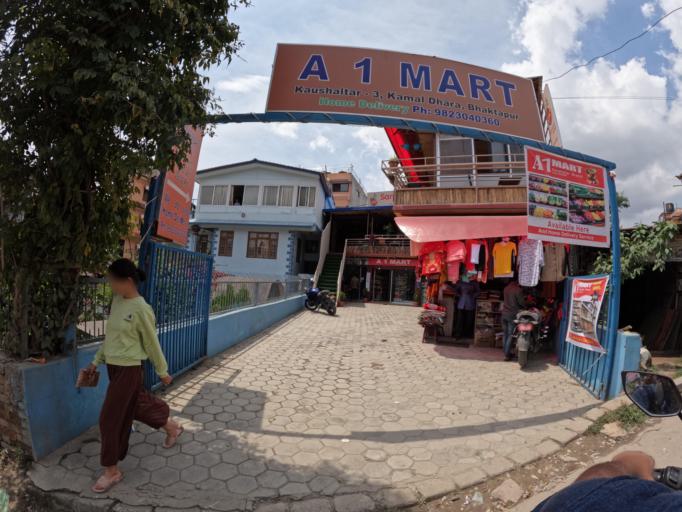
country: NP
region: Central Region
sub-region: Bagmati Zone
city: Kathmandu
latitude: 27.6768
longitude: 85.3657
